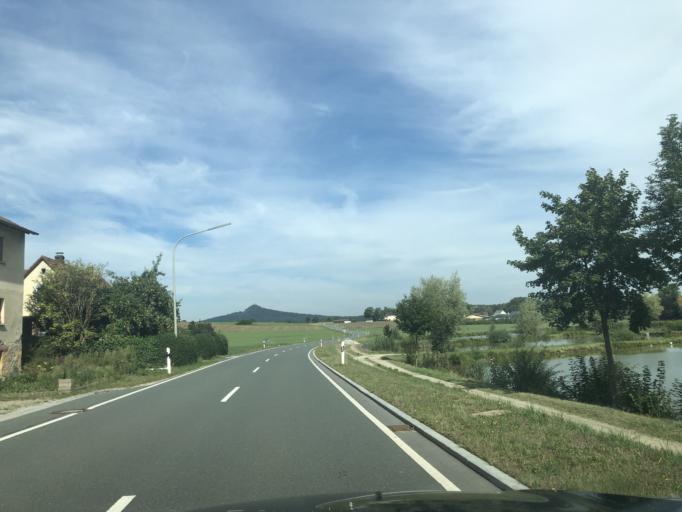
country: DE
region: Bavaria
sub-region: Upper Palatinate
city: Trabitz
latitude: 49.7910
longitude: 11.8895
